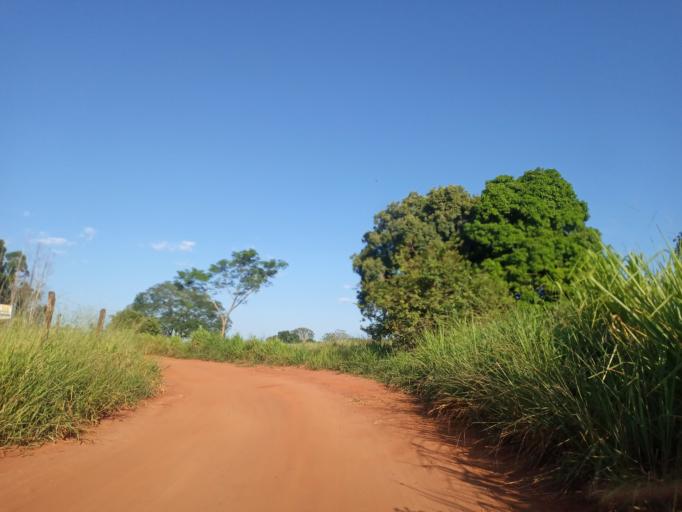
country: BR
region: Minas Gerais
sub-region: Ituiutaba
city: Ituiutaba
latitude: -18.9774
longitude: -49.5024
